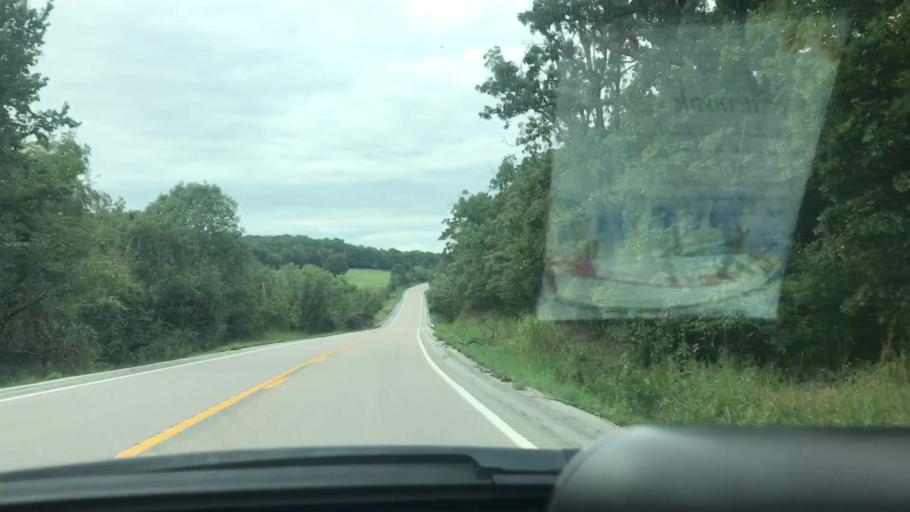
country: US
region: Missouri
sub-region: Benton County
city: Warsaw
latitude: 38.1212
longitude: -93.2776
